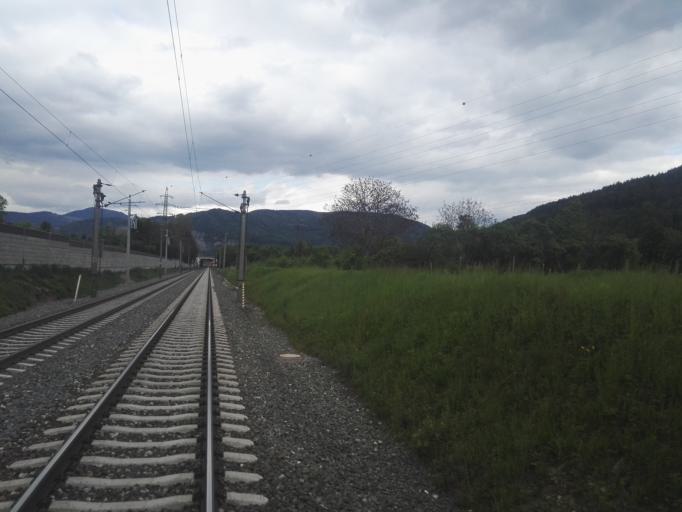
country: AT
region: Styria
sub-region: Politischer Bezirk Graz-Umgebung
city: Deutschfeistritz
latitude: 47.1815
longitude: 15.3276
